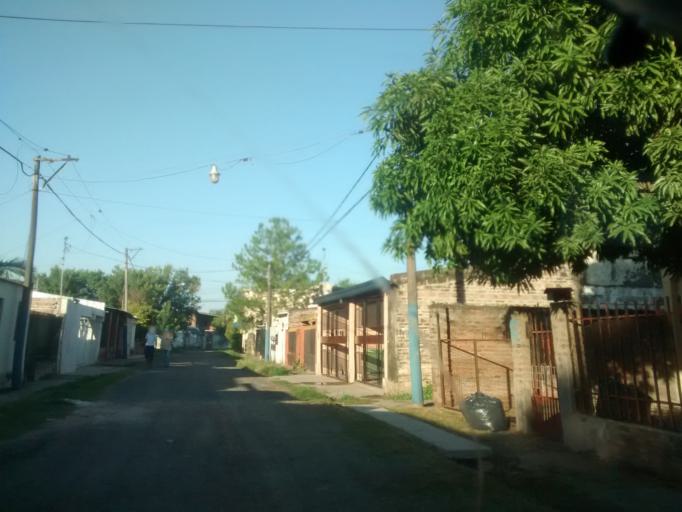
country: AR
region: Chaco
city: Resistencia
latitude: -27.4711
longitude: -58.9898
